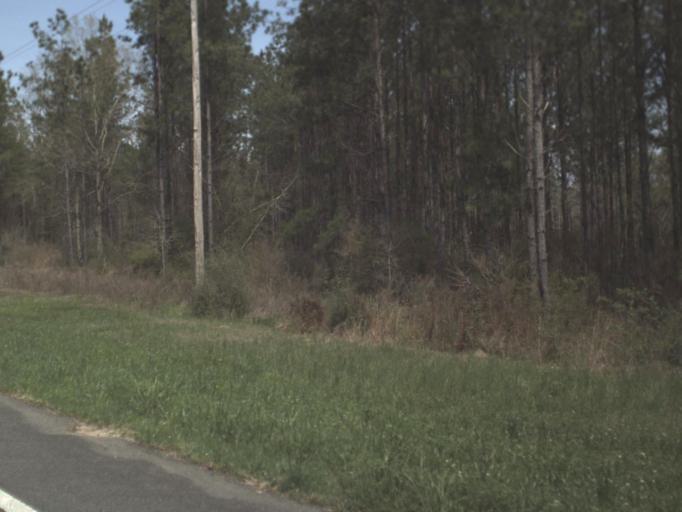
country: US
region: Alabama
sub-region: Geneva County
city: Geneva
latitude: 30.9196
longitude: -85.9615
